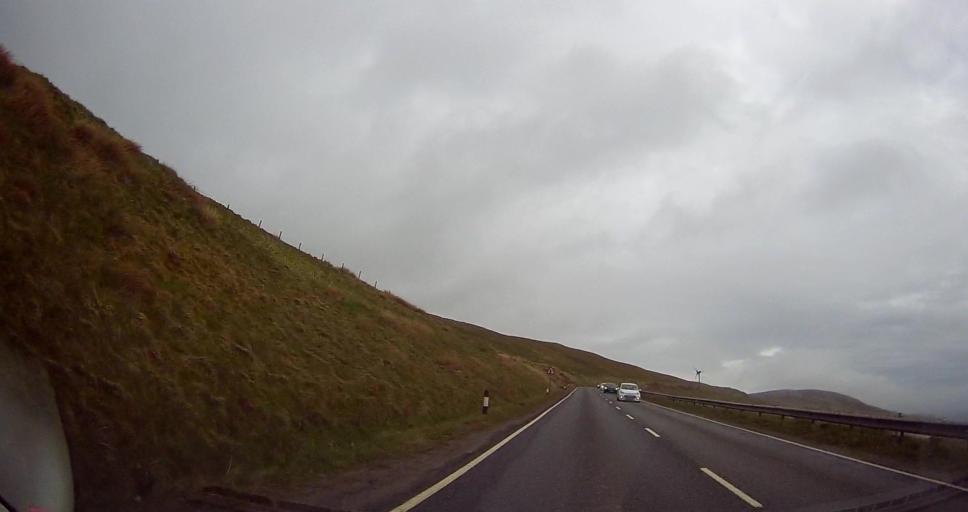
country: GB
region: Scotland
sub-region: Shetland Islands
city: Lerwick
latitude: 60.1644
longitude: -1.2276
